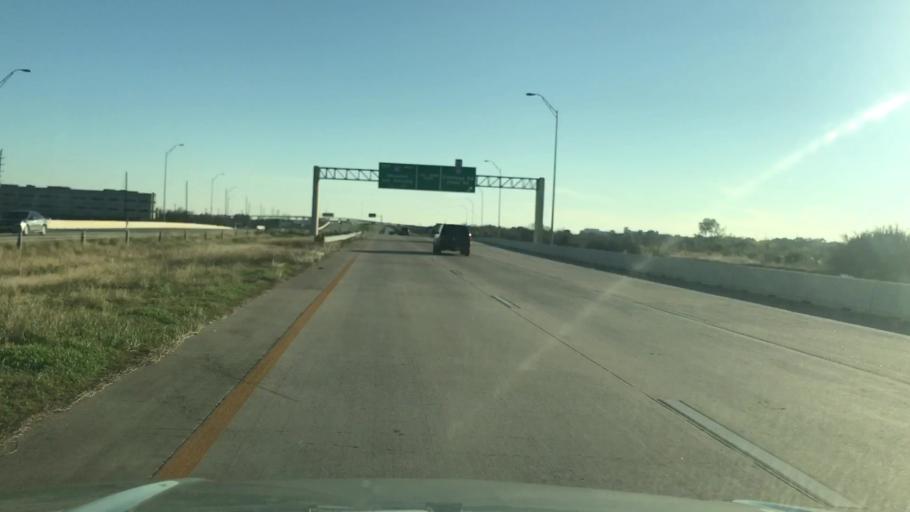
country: US
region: Texas
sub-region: Harris County
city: Katy
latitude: 29.8084
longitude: -95.7744
